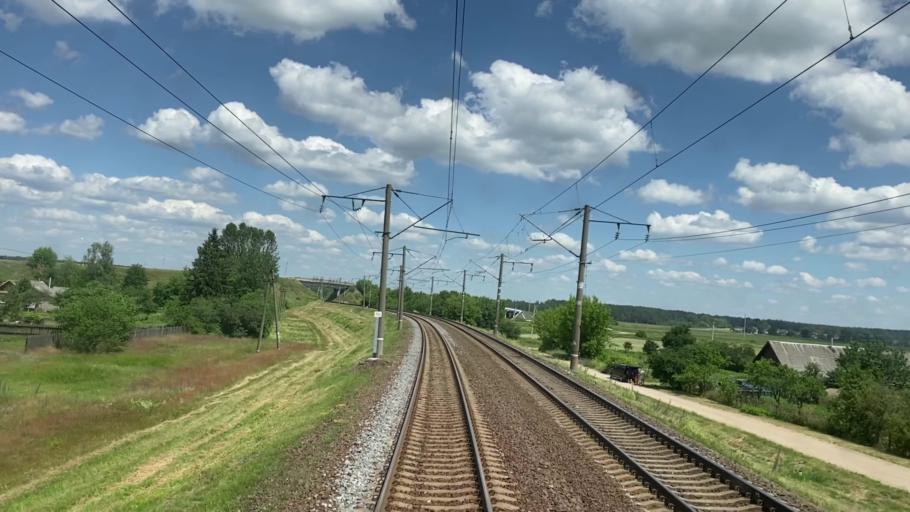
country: BY
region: Brest
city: Ivatsevichy
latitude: 52.7152
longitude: 25.3559
